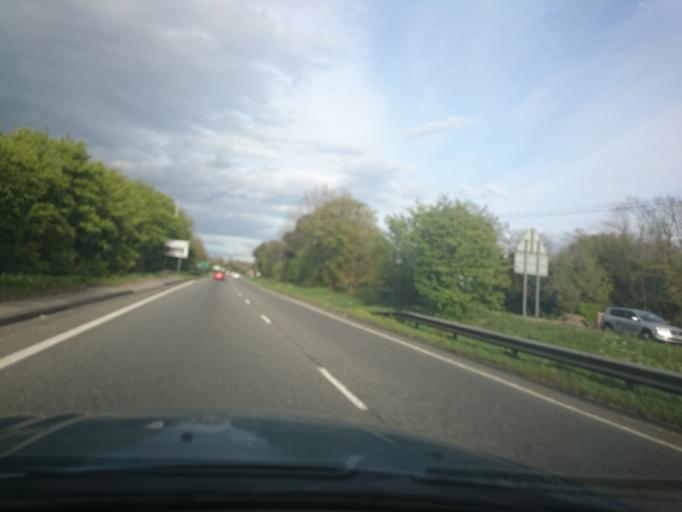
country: GB
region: England
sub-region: Surrey
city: Seale
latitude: 51.2266
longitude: -0.7169
